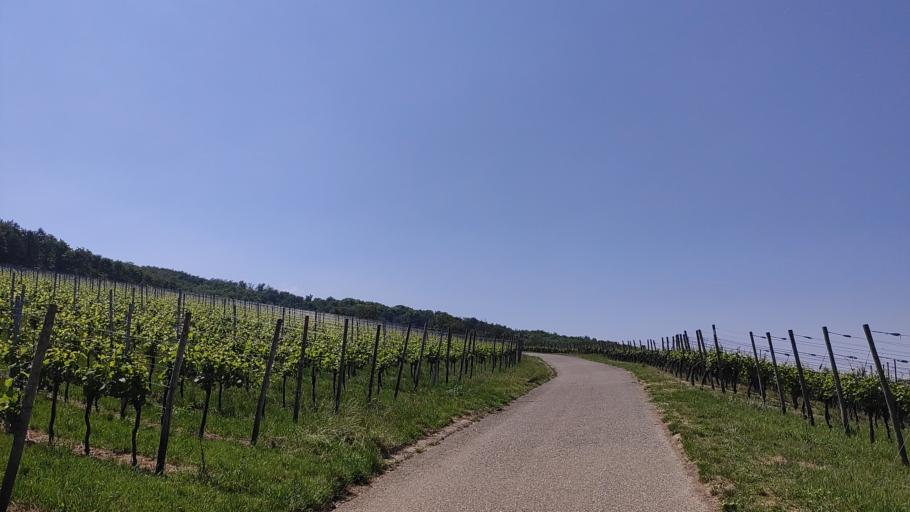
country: DE
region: Baden-Wuerttemberg
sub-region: Freiburg Region
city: Ebringen
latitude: 47.9503
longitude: 7.7668
